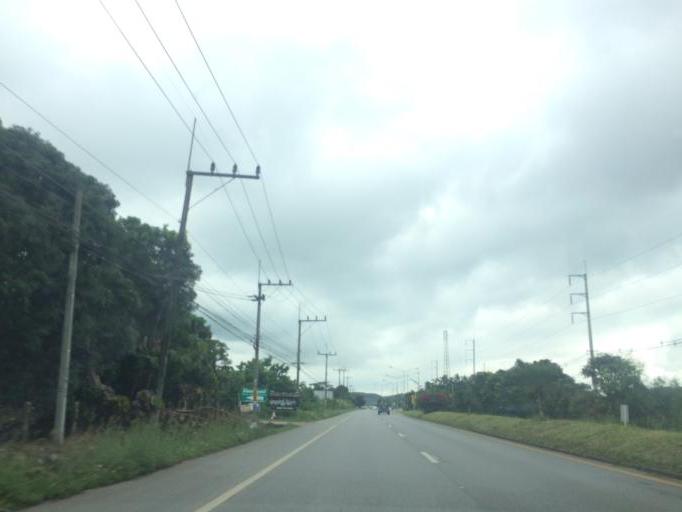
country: TH
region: Chiang Rai
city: Mae Chan
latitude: 20.0917
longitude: 99.8748
